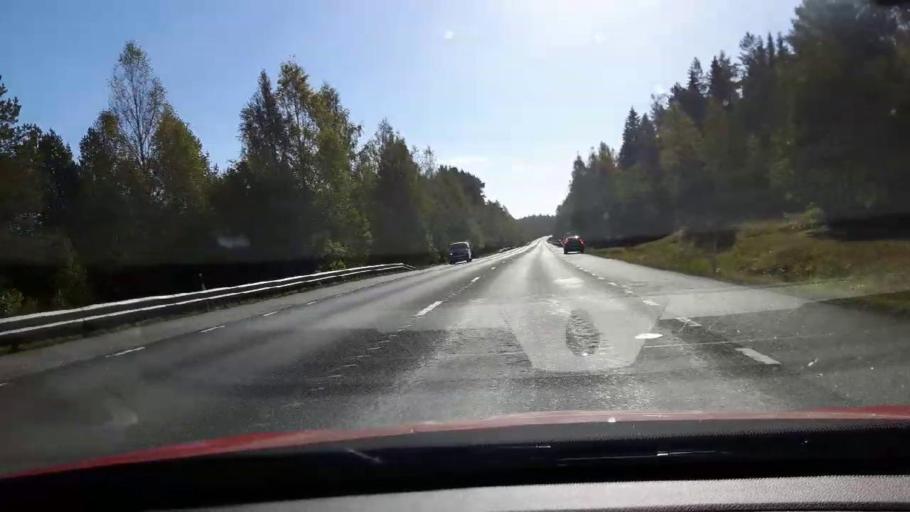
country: SE
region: Jaemtland
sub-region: Braecke Kommun
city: Braecke
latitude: 62.6991
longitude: 15.5215
